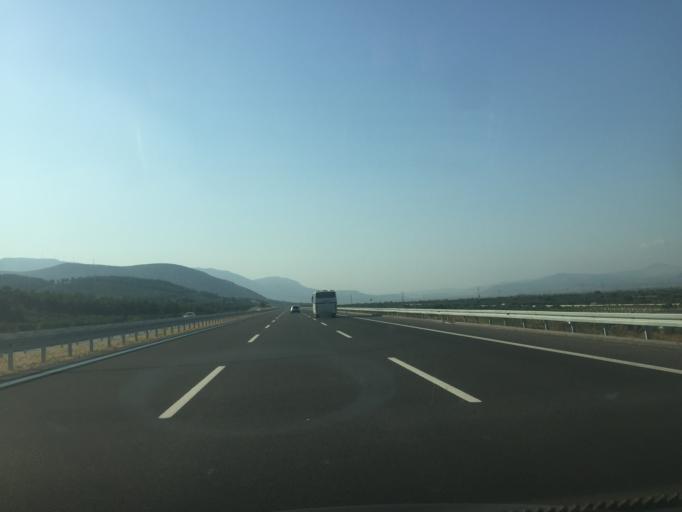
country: TR
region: Manisa
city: Zeytinliova
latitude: 39.0469
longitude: 27.7368
